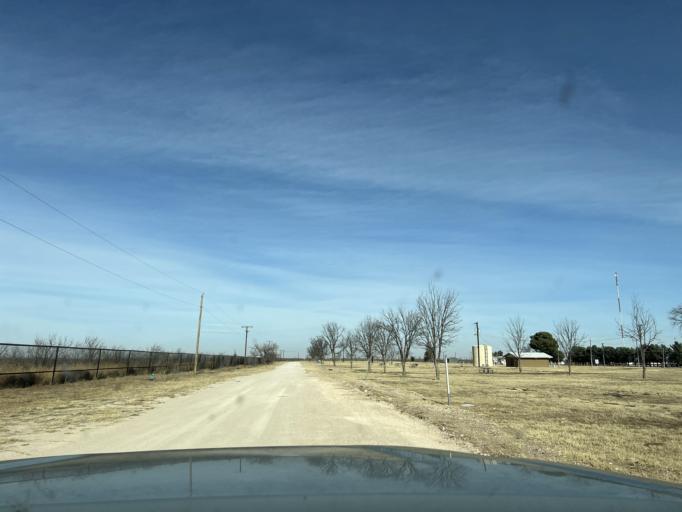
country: US
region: Texas
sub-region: Andrews County
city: Andrews
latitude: 32.4532
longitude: -102.5715
